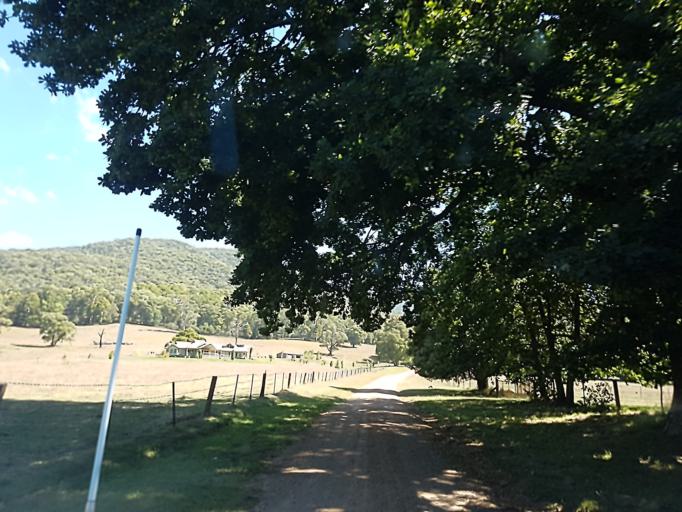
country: AU
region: Victoria
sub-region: Alpine
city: Mount Beauty
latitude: -36.8724
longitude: 147.0604
